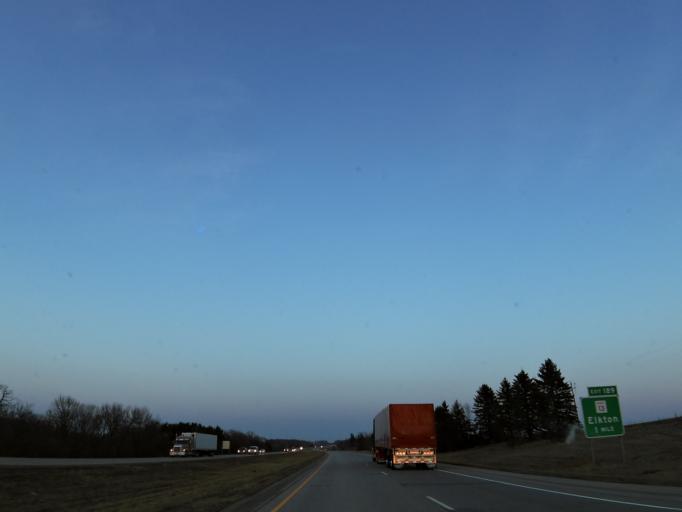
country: US
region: Minnesota
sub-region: Mower County
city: Austin
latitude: 43.6735
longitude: -92.7740
